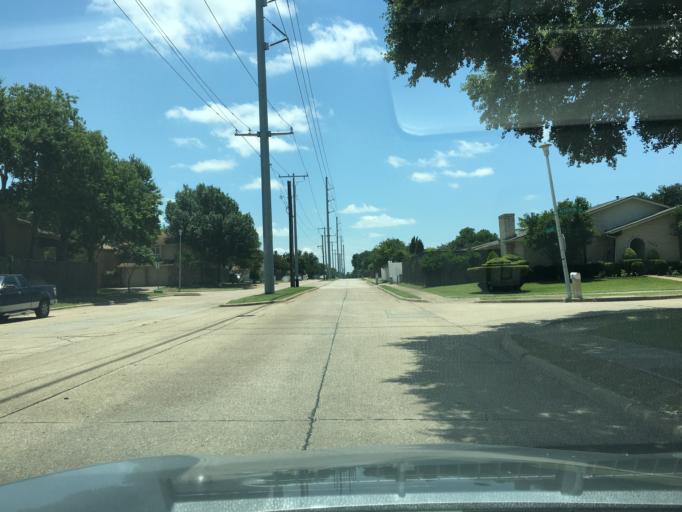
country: US
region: Texas
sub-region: Dallas County
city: Garland
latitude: 32.9507
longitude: -96.6736
